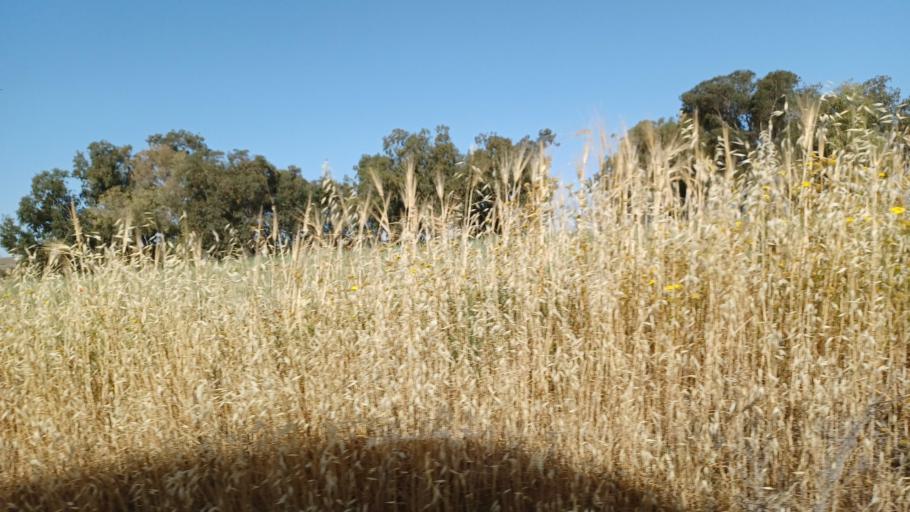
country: CY
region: Lefkosia
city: Mammari
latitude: 35.1690
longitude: 33.2488
